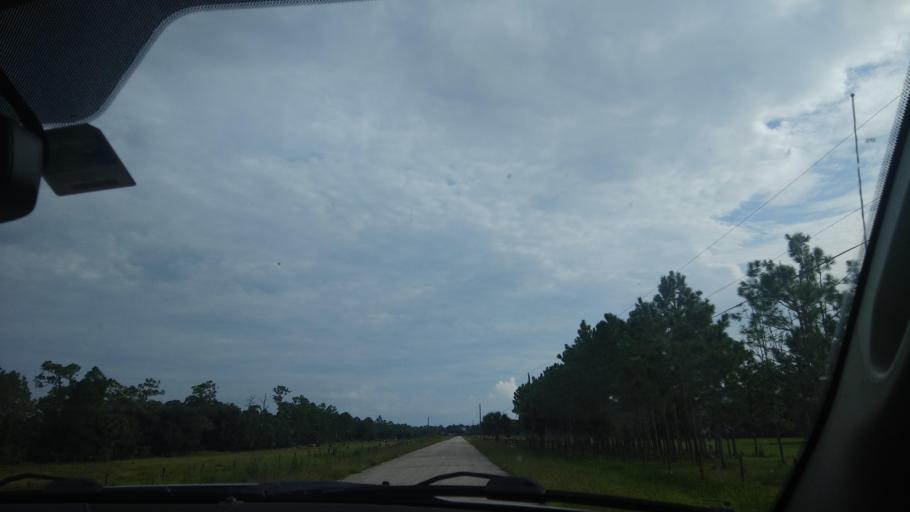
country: US
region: Florida
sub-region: Indian River County
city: Fellsmere
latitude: 27.6718
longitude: -80.8023
